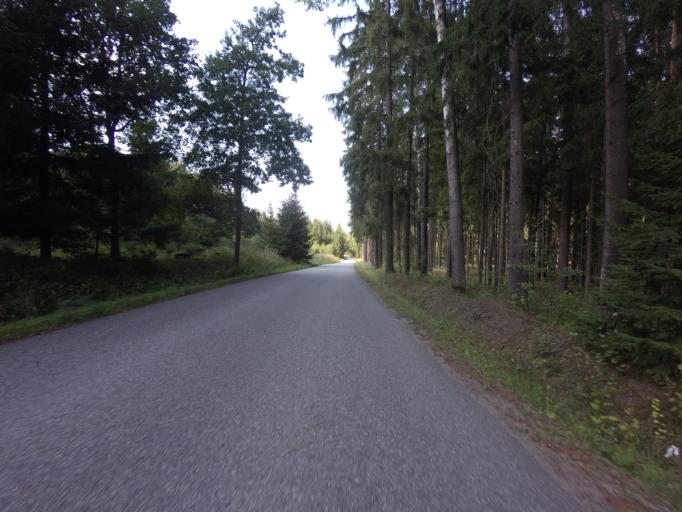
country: CZ
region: Jihocesky
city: Tyn nad Vltavou
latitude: 49.1616
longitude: 14.4293
